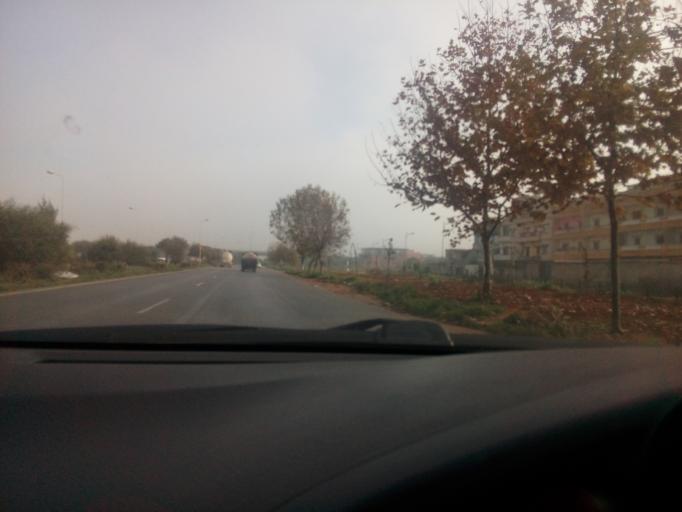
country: DZ
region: Oran
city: Es Senia
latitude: 35.6561
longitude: -0.6211
